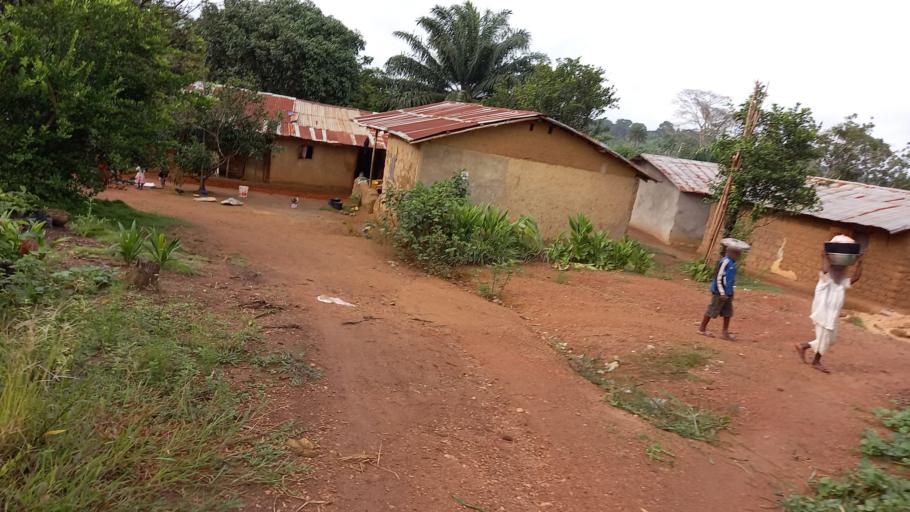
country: SL
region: Eastern Province
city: Kailahun
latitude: 8.2754
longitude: -10.5837
